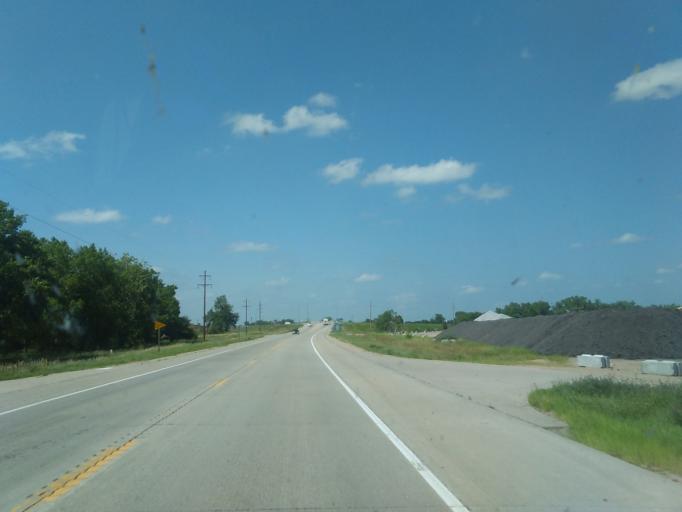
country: US
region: Nebraska
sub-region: Phelps County
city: Holdrege
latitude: 40.6849
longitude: -99.3802
